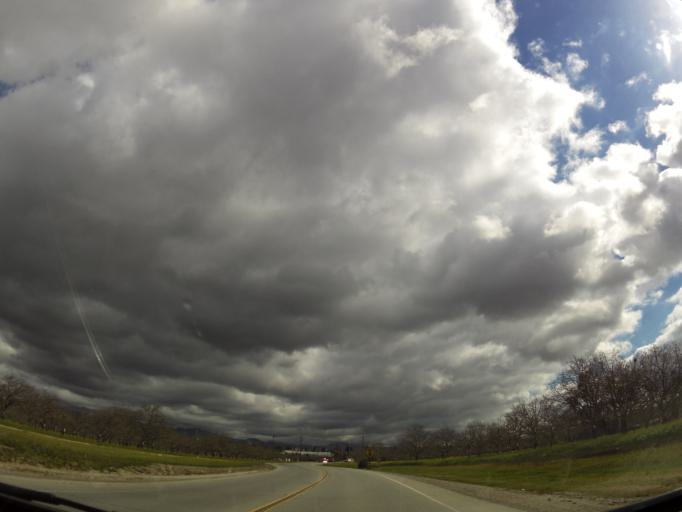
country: US
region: California
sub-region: San Benito County
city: Hollister
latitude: 36.8268
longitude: -121.3908
